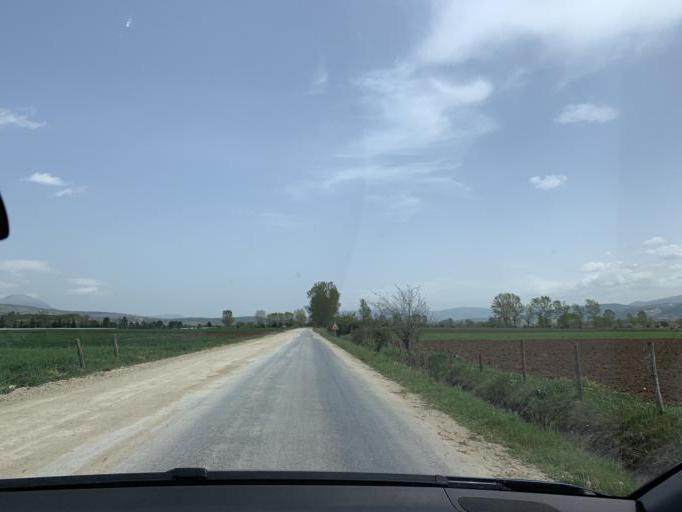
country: TR
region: Bolu
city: Bolu
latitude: 40.7464
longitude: 31.6613
